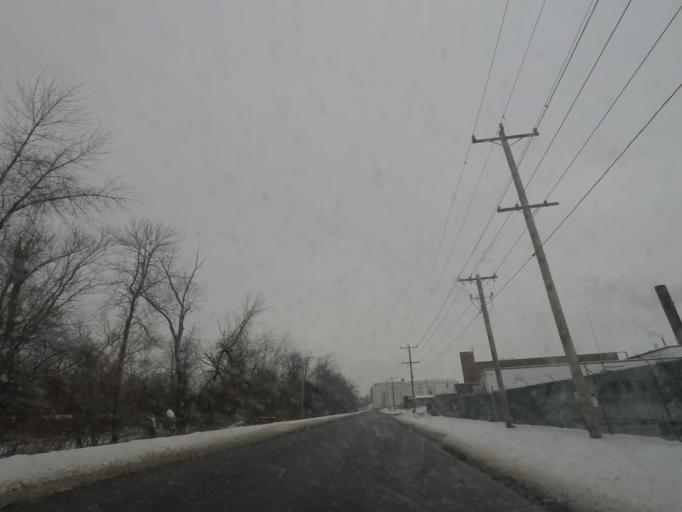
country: US
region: New York
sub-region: Rensselaer County
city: Rensselaer
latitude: 42.6164
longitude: -73.7641
